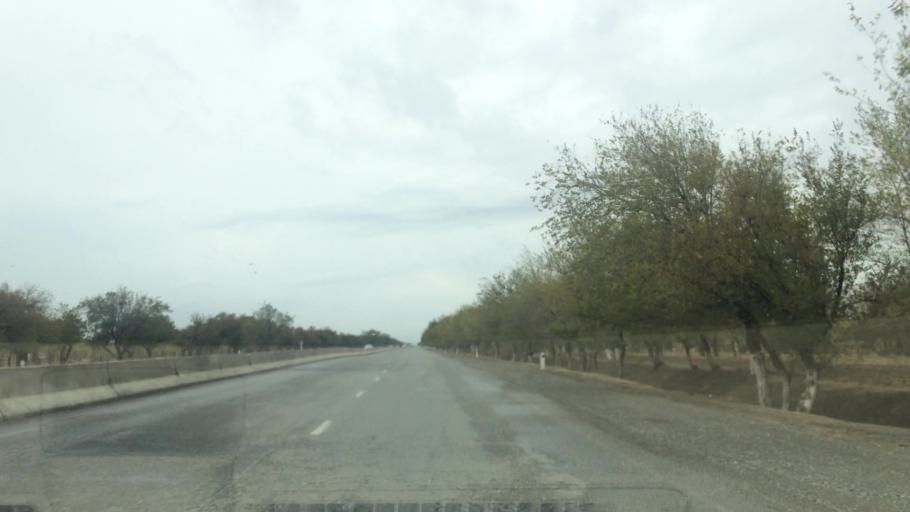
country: UZ
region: Samarqand
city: Bulung'ur
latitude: 39.8351
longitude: 67.4226
